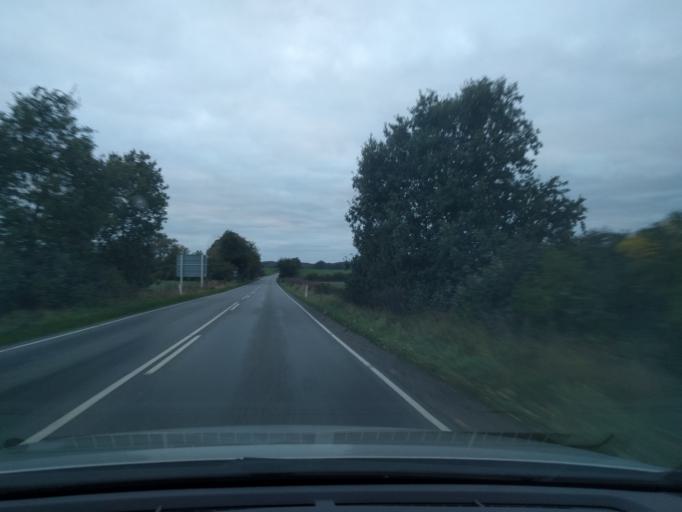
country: DK
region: South Denmark
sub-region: Odense Kommune
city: Bellinge
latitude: 55.2111
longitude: 10.3318
